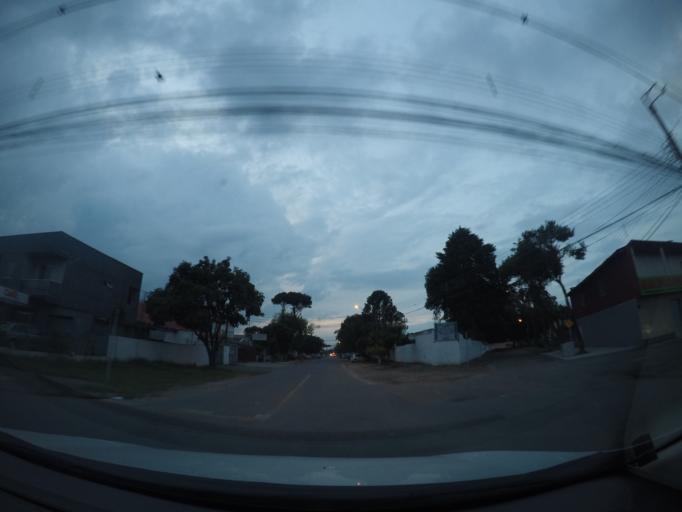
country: BR
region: Parana
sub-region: Sao Jose Dos Pinhais
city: Sao Jose dos Pinhais
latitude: -25.5039
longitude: -49.2281
